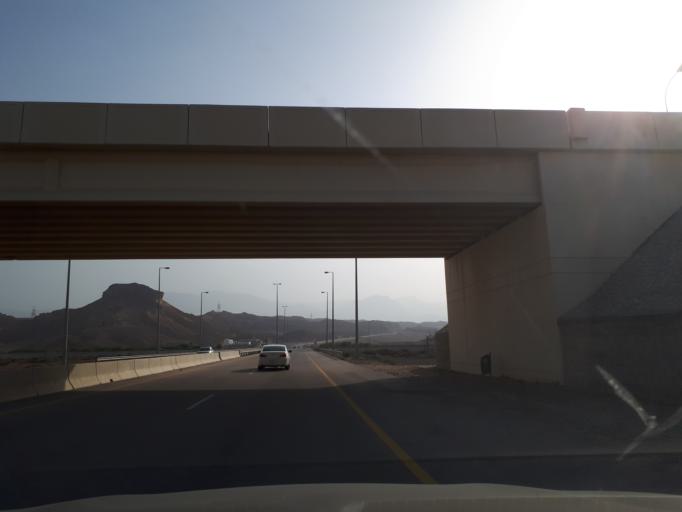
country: OM
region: Muhafazat Masqat
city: Muscat
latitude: 23.2116
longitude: 58.9269
